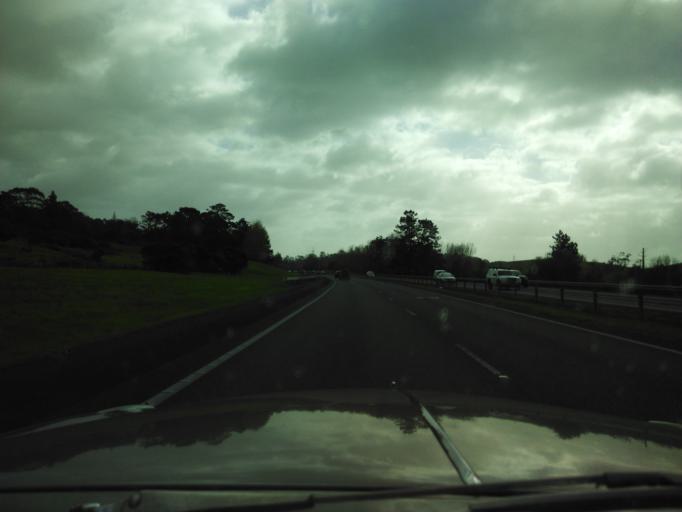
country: NZ
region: Auckland
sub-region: Auckland
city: Rothesay Bay
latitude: -36.6706
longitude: 174.6815
